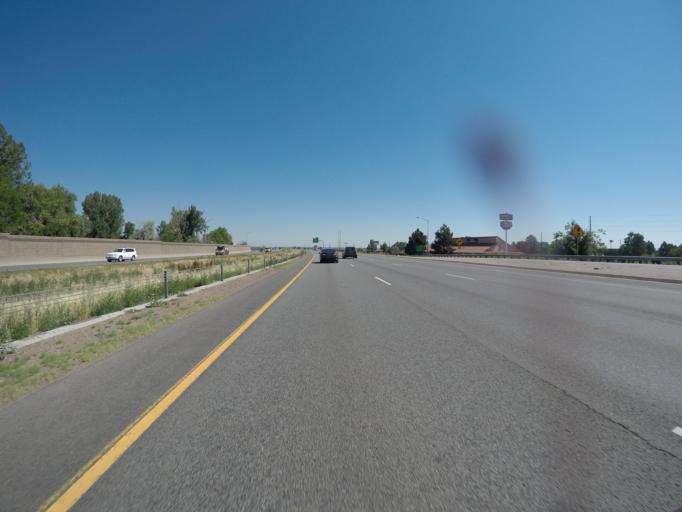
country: US
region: Colorado
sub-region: Jefferson County
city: Applewood
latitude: 39.7578
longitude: -105.1437
